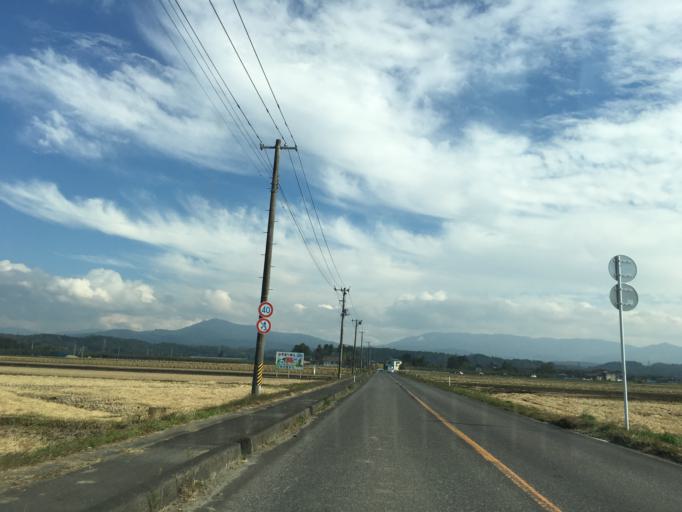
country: JP
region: Fukushima
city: Sukagawa
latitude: 37.2793
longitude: 140.3985
